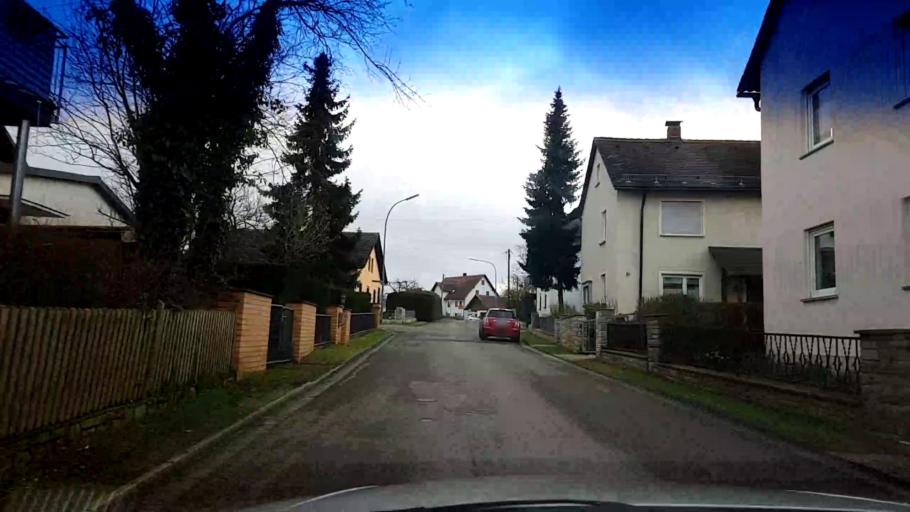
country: DE
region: Bavaria
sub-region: Upper Franconia
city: Litzendorf
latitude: 49.9068
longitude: 11.0022
